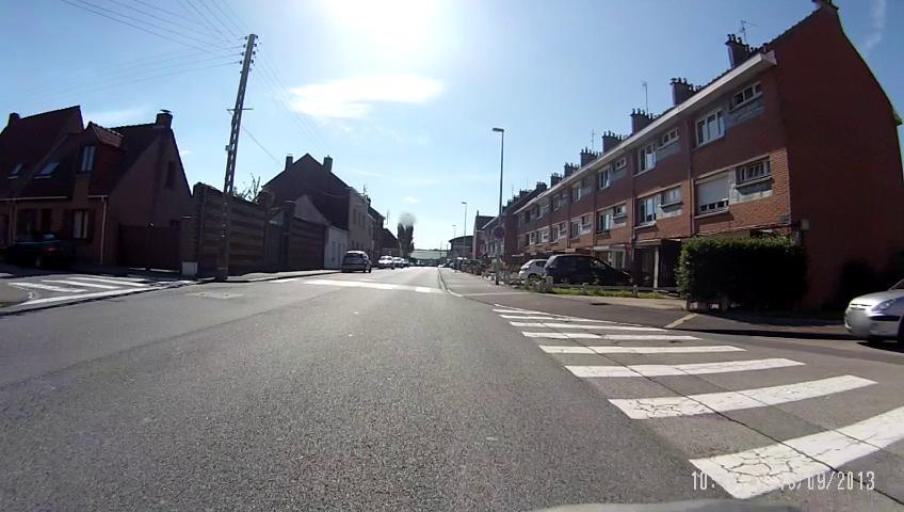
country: FR
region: Nord-Pas-de-Calais
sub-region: Departement du Nord
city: Teteghem
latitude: 51.0492
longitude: 2.4330
